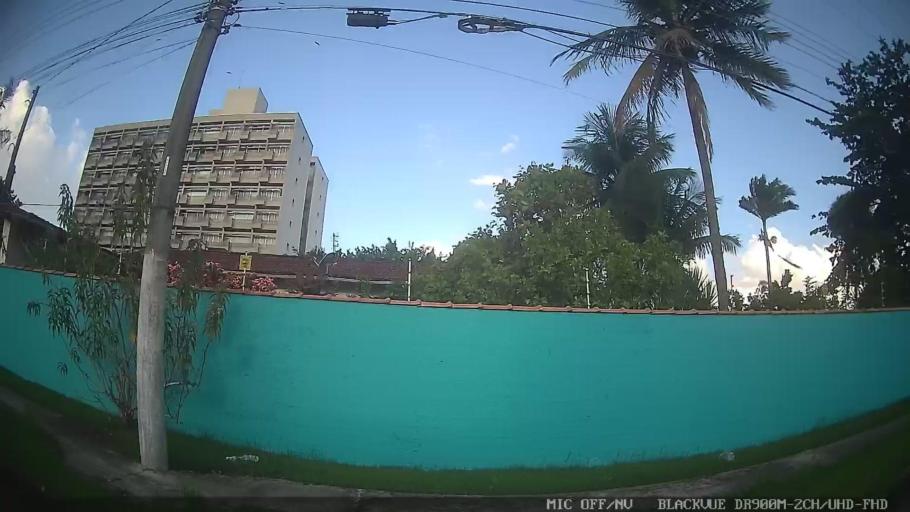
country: BR
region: Sao Paulo
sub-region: Caraguatatuba
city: Caraguatatuba
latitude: -23.6818
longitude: -45.4331
